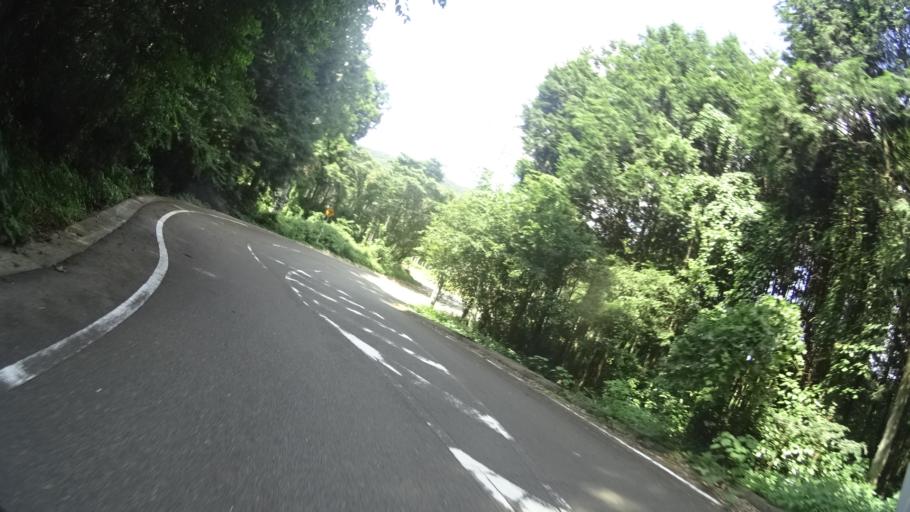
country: JP
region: Yamaguchi
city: Hagi
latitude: 34.4984
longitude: 131.5559
